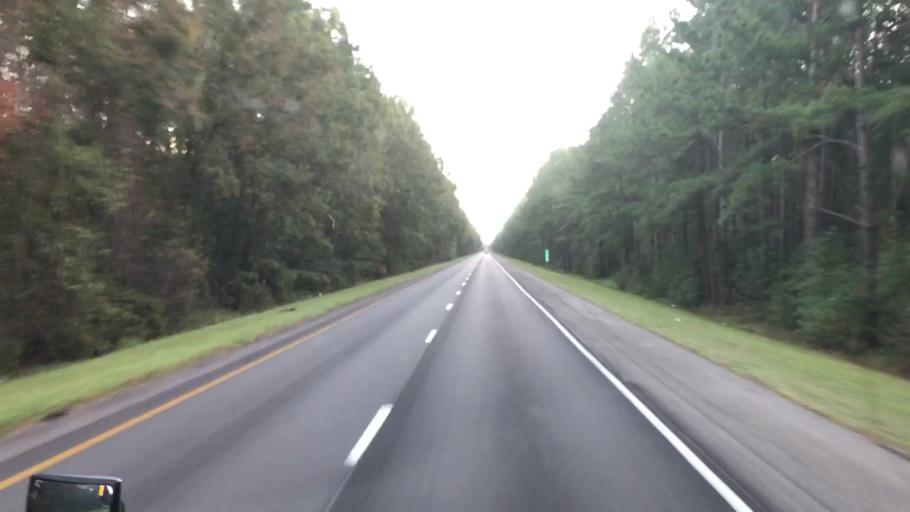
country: US
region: South Carolina
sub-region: Orangeburg County
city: Holly Hill
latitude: 33.5371
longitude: -80.4178
